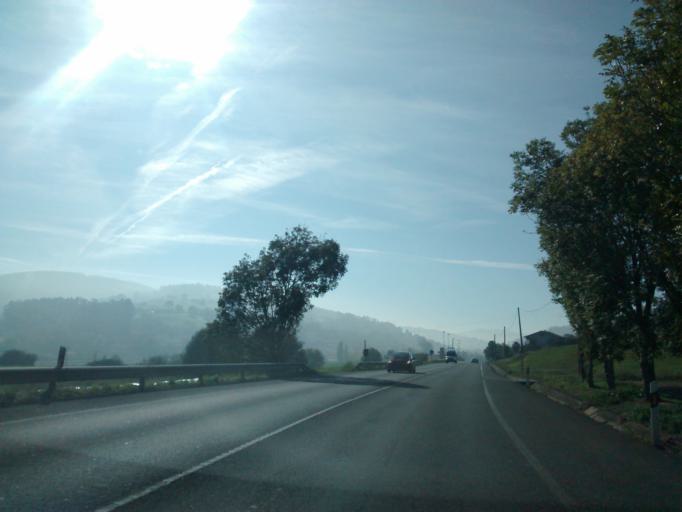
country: ES
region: Cantabria
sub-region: Provincia de Cantabria
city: Lierganes
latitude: 43.3617
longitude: -3.7643
